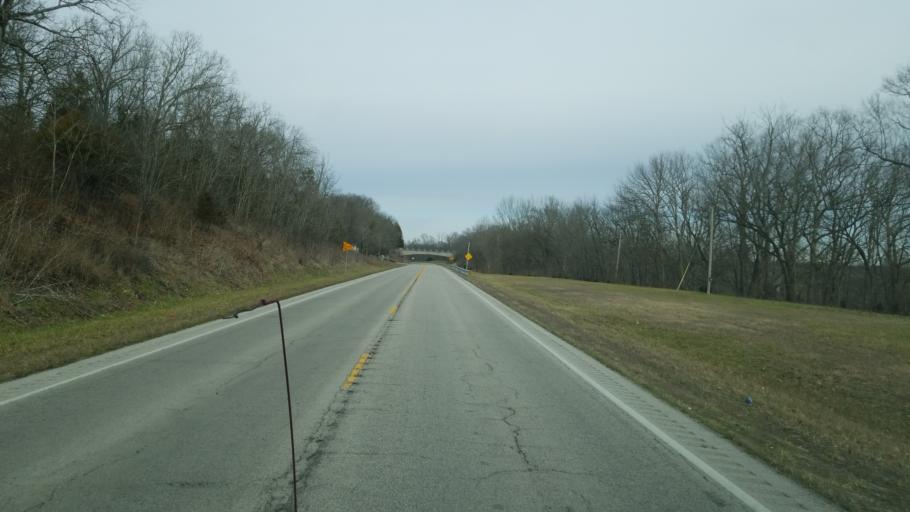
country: US
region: Kentucky
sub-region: Robertson County
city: Mount Olivet
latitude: 38.4269
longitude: -83.9928
